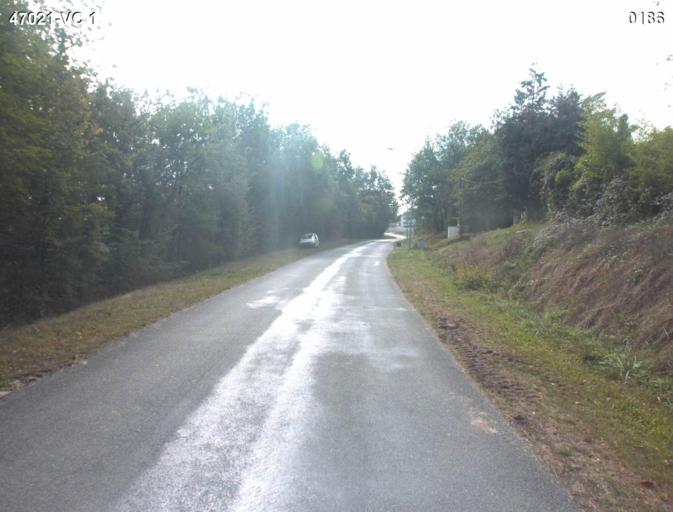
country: FR
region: Aquitaine
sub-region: Departement du Lot-et-Garonne
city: Barbaste
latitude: 44.1644
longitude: 0.2866
